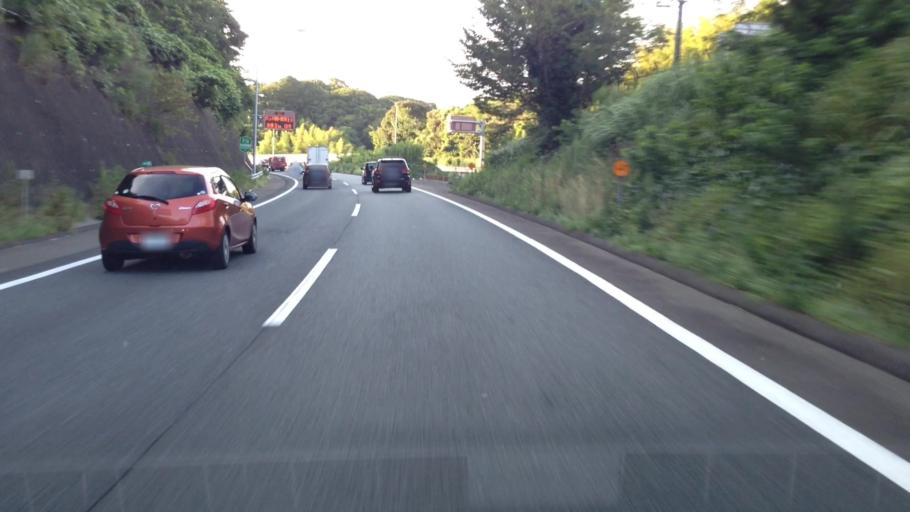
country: JP
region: Kanagawa
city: Kamakura
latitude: 35.3633
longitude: 139.5985
